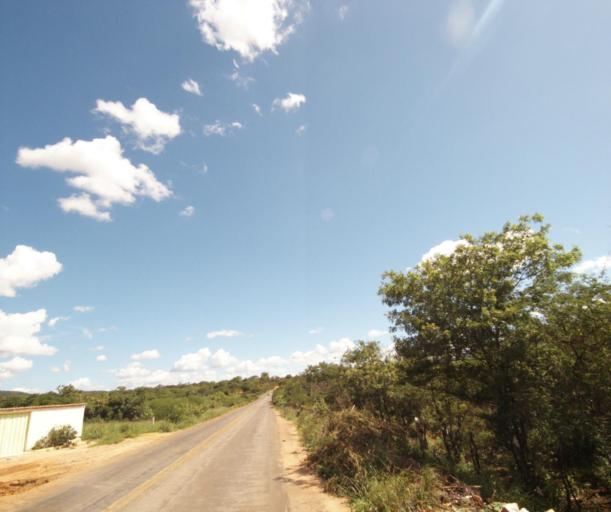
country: BR
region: Bahia
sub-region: Caetite
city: Caetite
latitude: -14.1711
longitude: -42.2297
